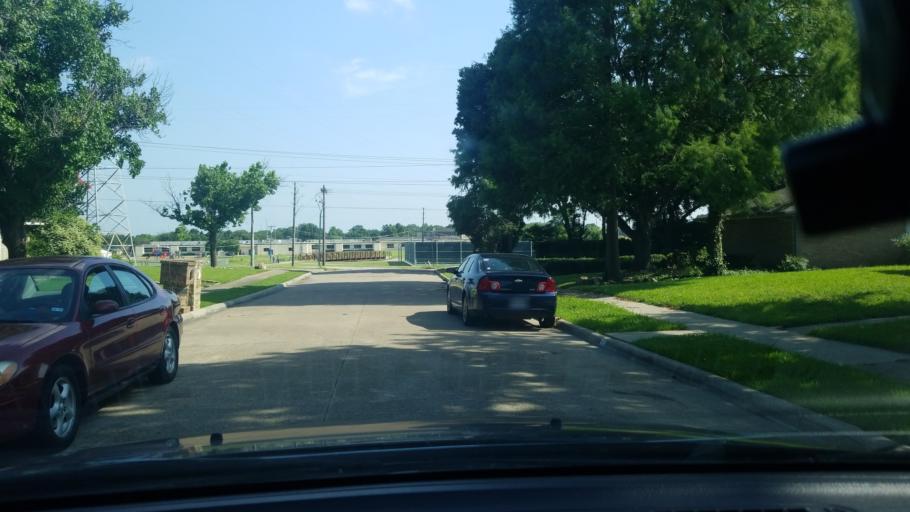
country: US
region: Texas
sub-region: Dallas County
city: Mesquite
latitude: 32.8202
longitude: -96.6118
